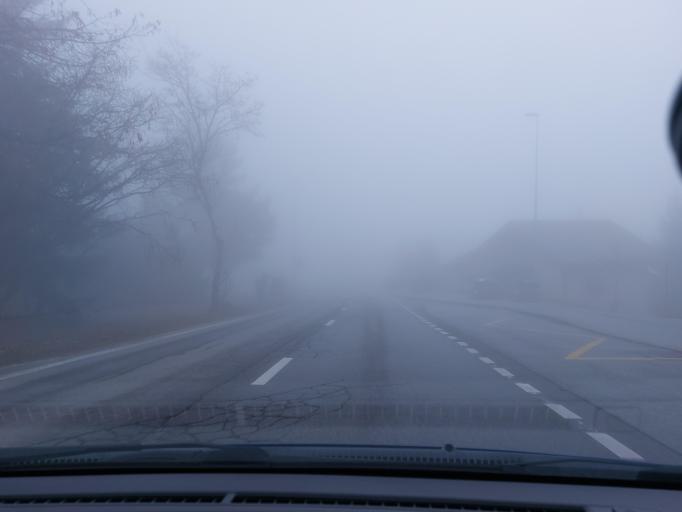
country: CH
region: Valais
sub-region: Sierre District
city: Randogne
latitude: 46.3161
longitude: 7.5003
